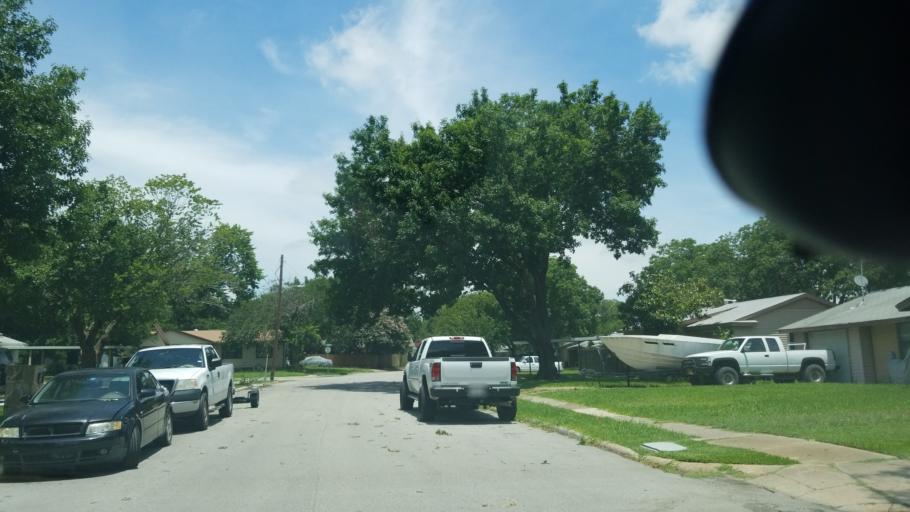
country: US
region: Texas
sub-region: Dallas County
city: Irving
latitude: 32.8473
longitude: -96.9742
